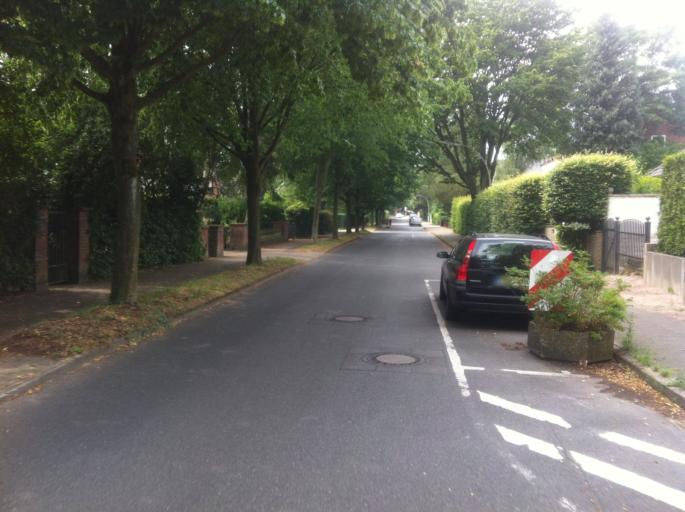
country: DE
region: Hamburg
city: Farmsen-Berne
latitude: 53.6239
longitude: 10.1446
